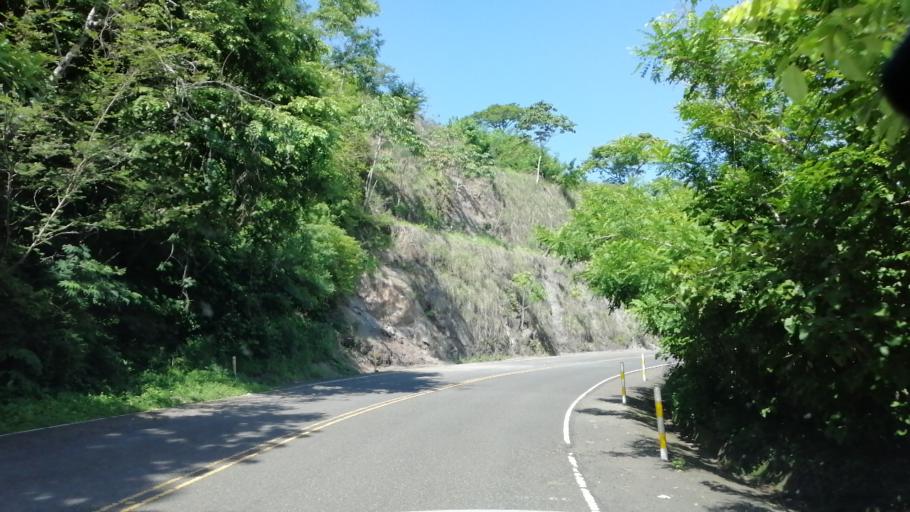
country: HN
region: Lempira
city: La Virtud
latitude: 13.9786
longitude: -88.7572
